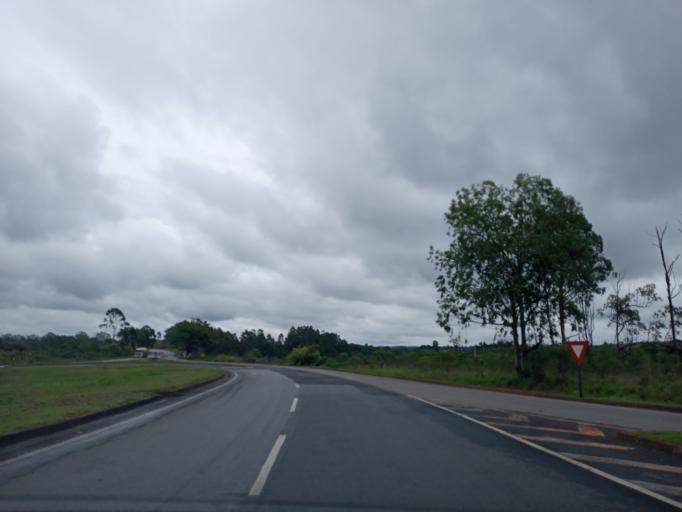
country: BR
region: Minas Gerais
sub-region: Campos Altos
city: Campos Altos
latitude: -19.6488
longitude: -46.0706
